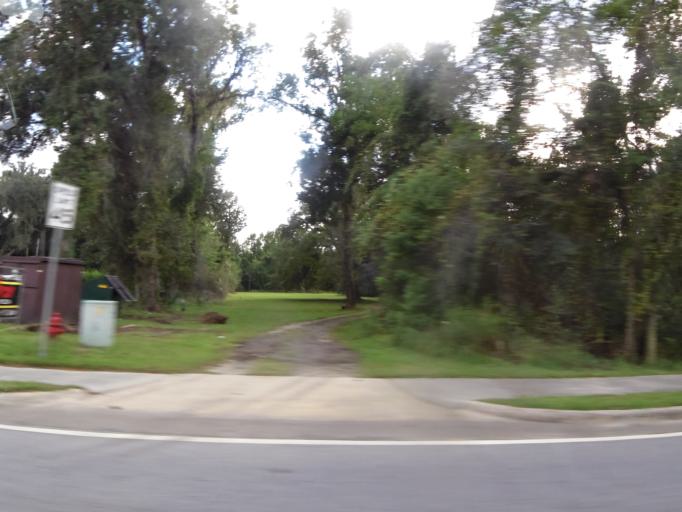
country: US
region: Georgia
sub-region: Liberty County
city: Midway
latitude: 31.7399
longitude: -81.4377
